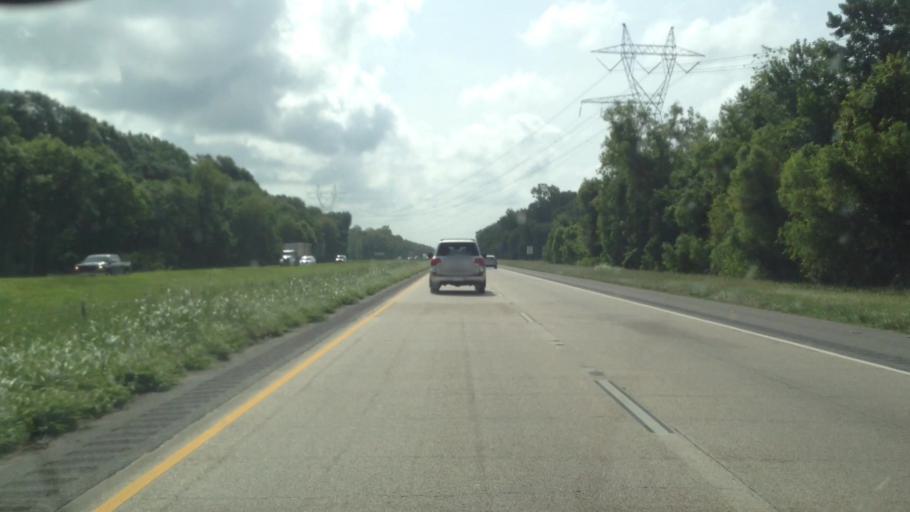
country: US
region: Louisiana
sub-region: Ascension Parish
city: Sorrento
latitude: 30.1684
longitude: -90.8660
